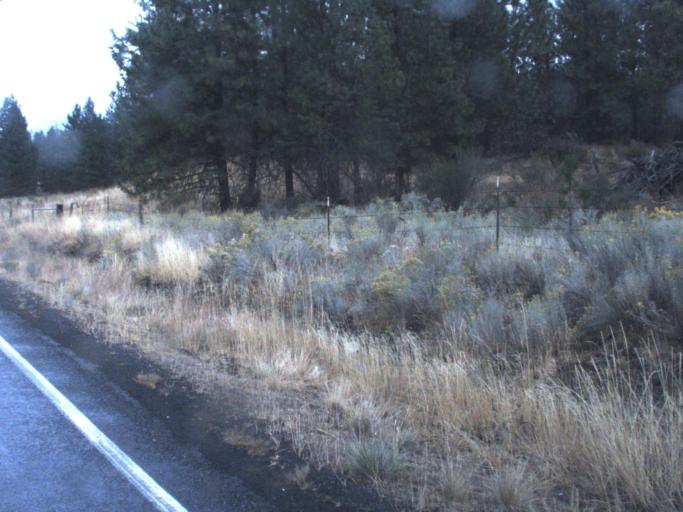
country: US
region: Washington
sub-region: Lincoln County
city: Davenport
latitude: 47.7961
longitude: -117.8912
